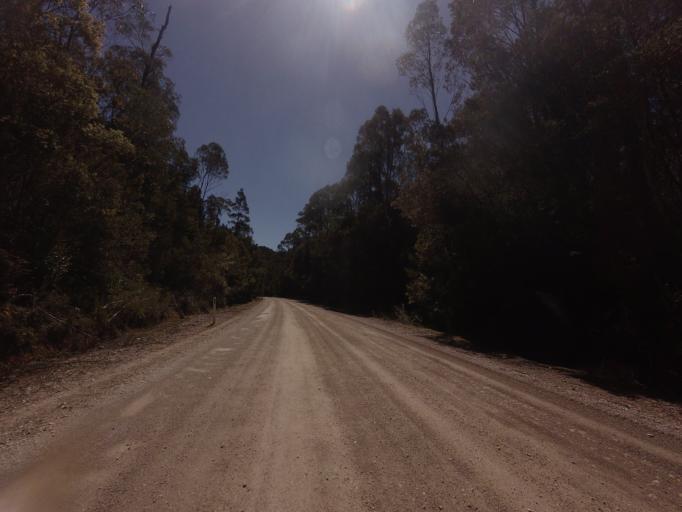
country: AU
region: Tasmania
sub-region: Huon Valley
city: Geeveston
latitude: -42.8228
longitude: 146.3900
